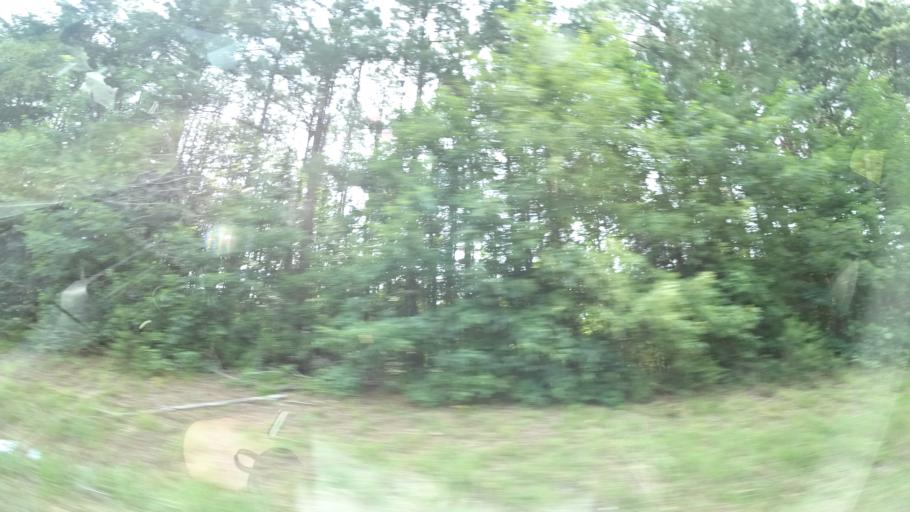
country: US
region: Virginia
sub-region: Spotsylvania County
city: Spotsylvania Courthouse
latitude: 38.1217
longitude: -77.7422
